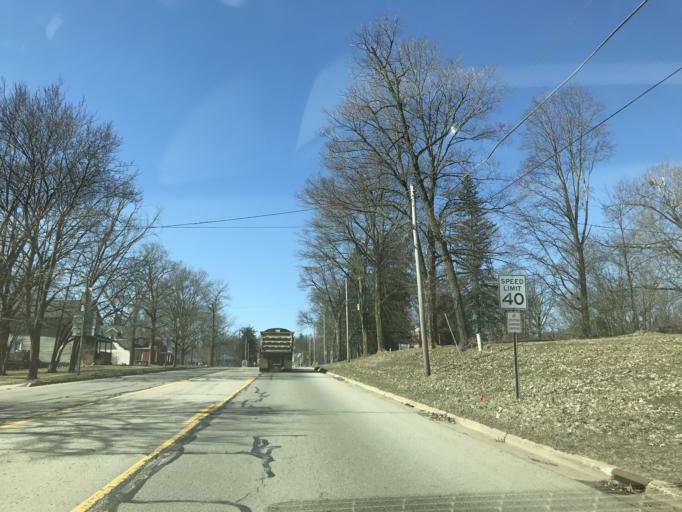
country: US
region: Michigan
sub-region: Hillsdale County
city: Jonesville
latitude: 41.9812
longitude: -84.6684
